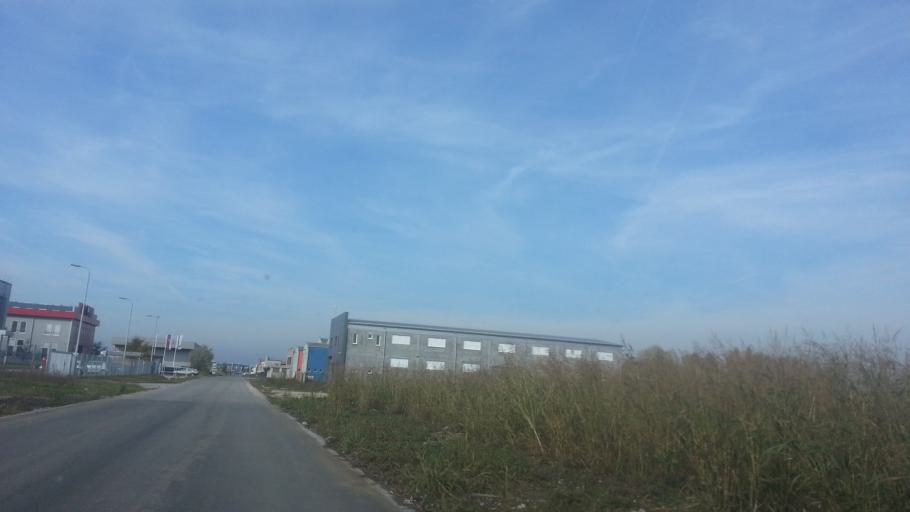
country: RS
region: Autonomna Pokrajina Vojvodina
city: Nova Pazova
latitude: 44.9499
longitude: 20.2016
